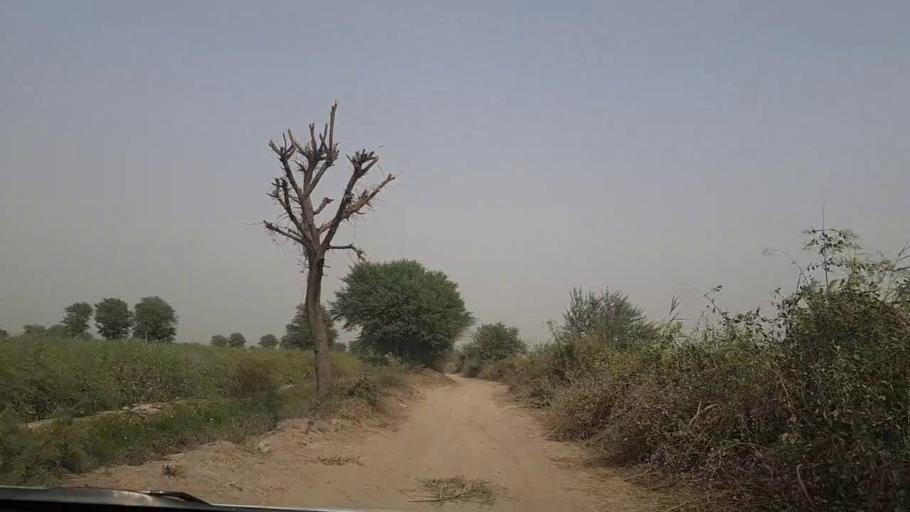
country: PK
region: Sindh
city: Pithoro
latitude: 25.4566
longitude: 69.2466
